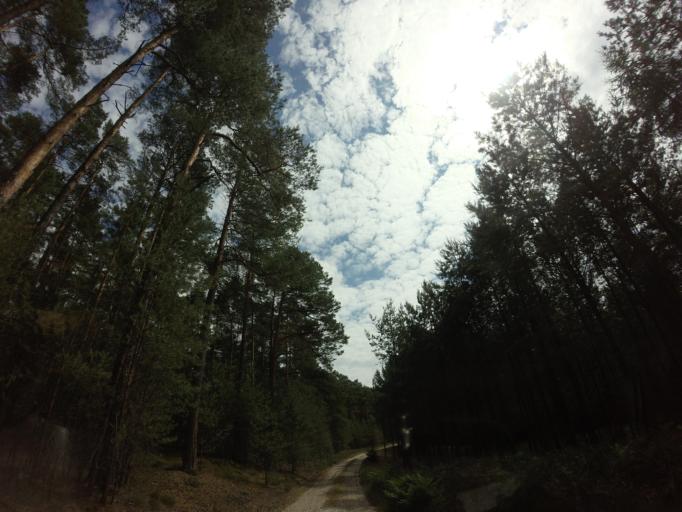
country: PL
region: West Pomeranian Voivodeship
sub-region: Powiat choszczenski
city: Drawno
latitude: 53.1571
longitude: 15.7580
